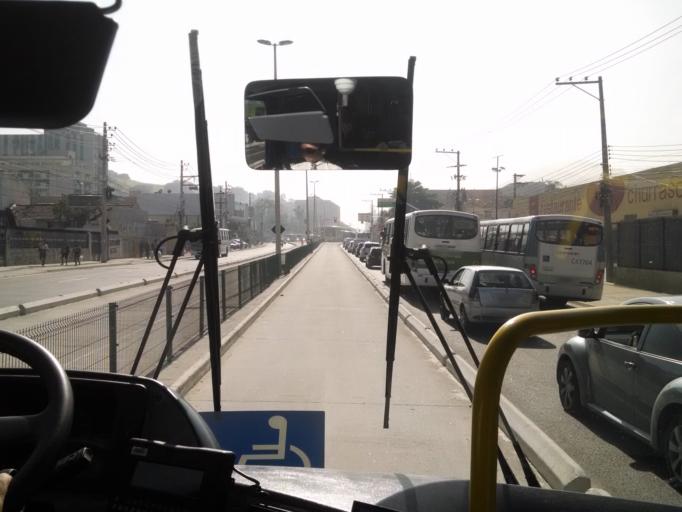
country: BR
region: Rio de Janeiro
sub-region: Sao Joao De Meriti
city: Sao Joao de Meriti
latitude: -22.8998
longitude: -43.3538
